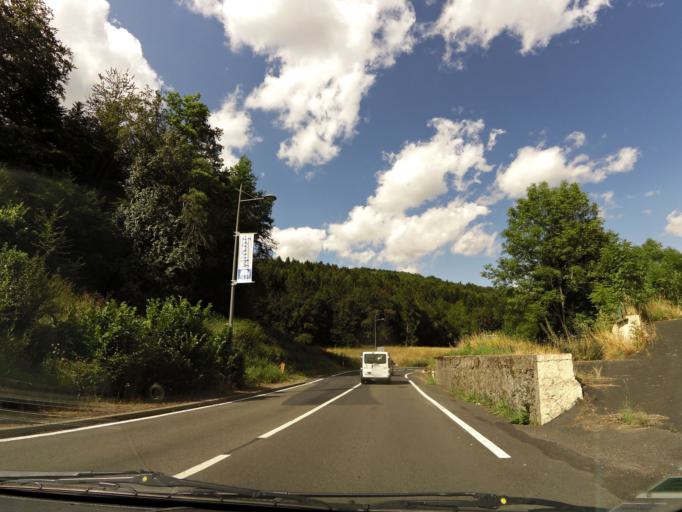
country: FR
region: Auvergne
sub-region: Departement du Puy-de-Dome
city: Aydat
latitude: 45.5746
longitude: 2.9281
